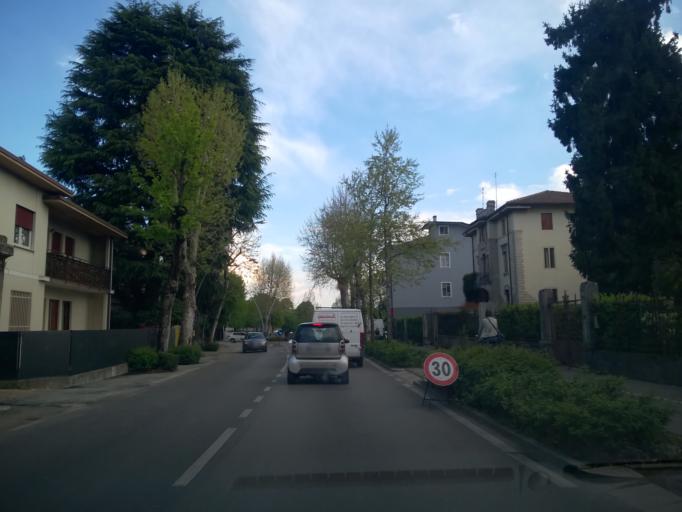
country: IT
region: Veneto
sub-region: Provincia di Vicenza
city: Thiene
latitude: 45.7091
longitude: 11.4835
